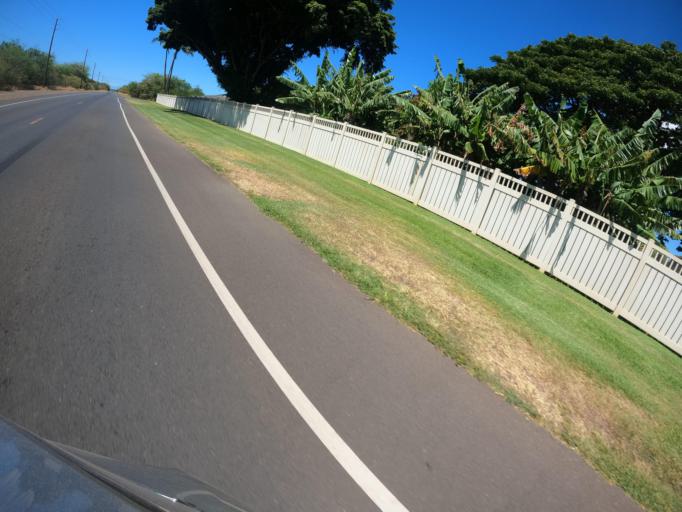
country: US
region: Hawaii
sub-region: Honolulu County
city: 'Ewa Villages
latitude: 21.3261
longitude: -158.0562
